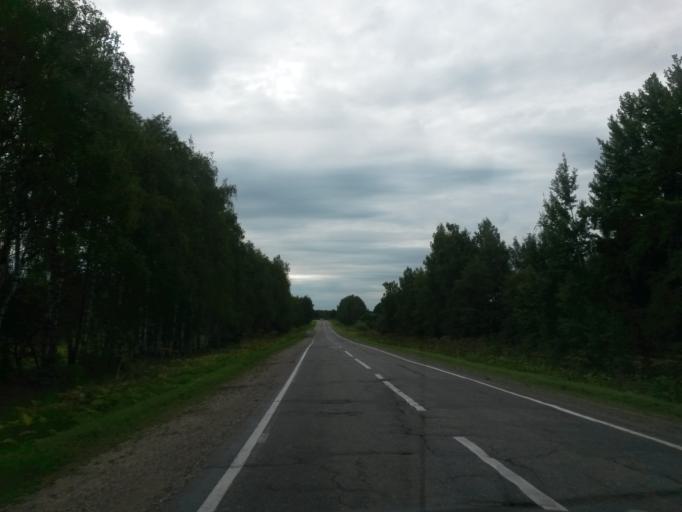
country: RU
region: Jaroslavl
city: Gavrilov-Yam
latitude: 57.3641
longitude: 39.7438
